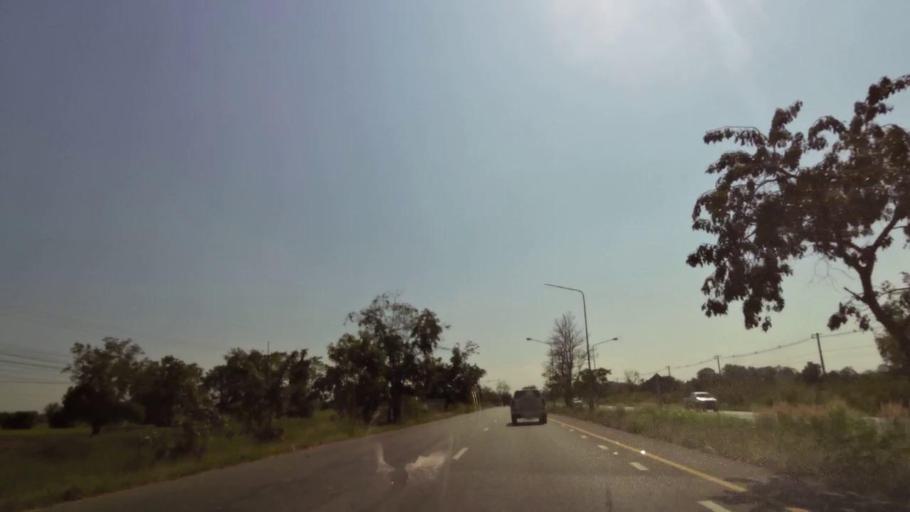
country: TH
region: Nakhon Sawan
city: Kao Liao
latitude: 15.8617
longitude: 100.1168
